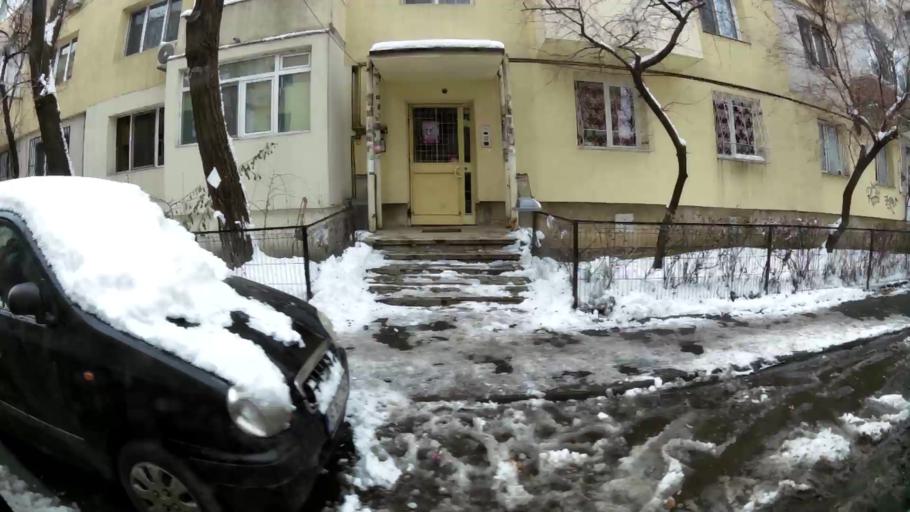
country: RO
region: Ilfov
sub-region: Comuna Popesti-Leordeni
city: Popesti-Leordeni
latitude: 44.3865
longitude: 26.1328
